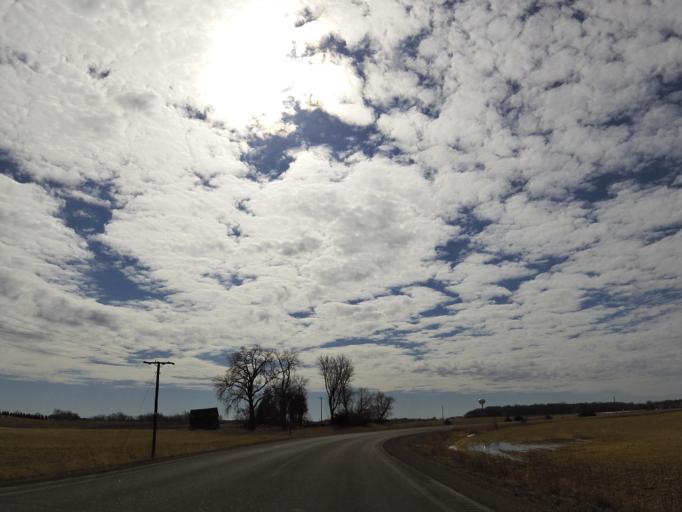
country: US
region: Minnesota
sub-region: Le Sueur County
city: New Prague
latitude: 44.5606
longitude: -93.5566
